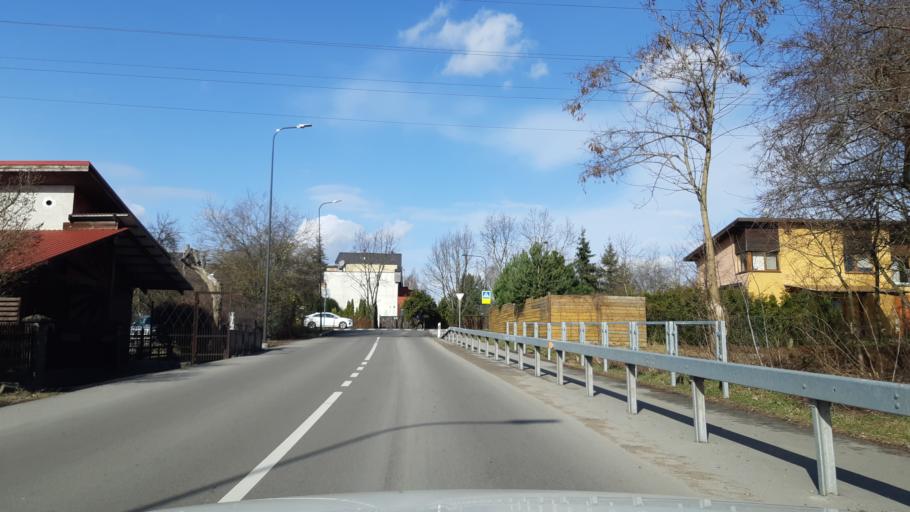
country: LT
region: Kauno apskritis
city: Dainava (Kaunas)
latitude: 54.8941
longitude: 23.9598
